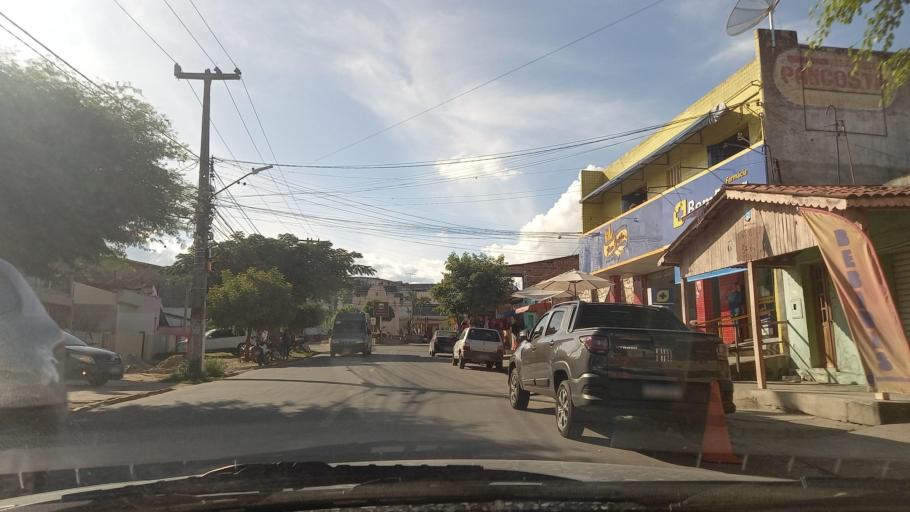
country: BR
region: Pernambuco
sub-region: Gravata
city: Gravata
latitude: -8.1983
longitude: -35.5725
